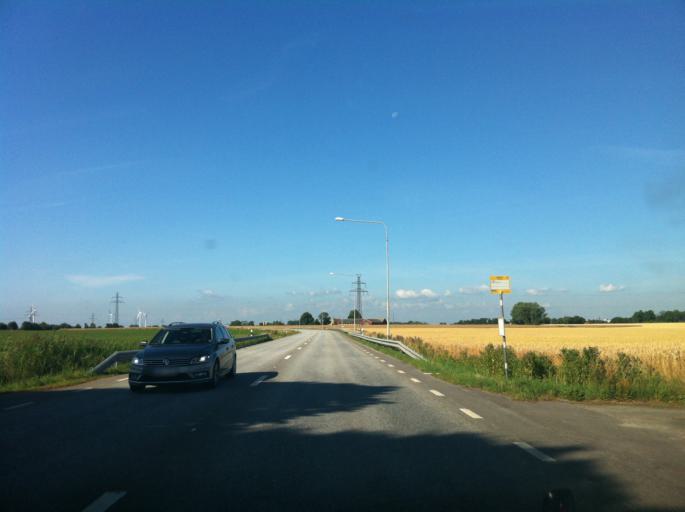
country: SE
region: Skane
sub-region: Landskrona
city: Asmundtorp
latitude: 55.8818
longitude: 12.9005
